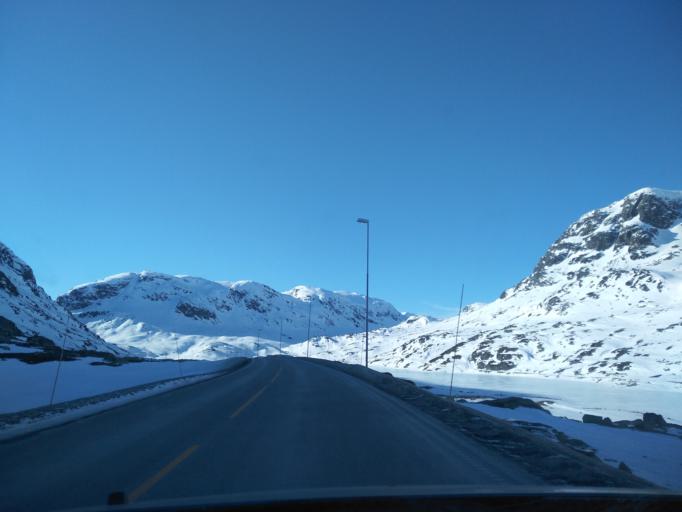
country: NO
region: Aust-Agder
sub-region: Bykle
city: Hovden
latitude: 59.8510
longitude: 7.1024
